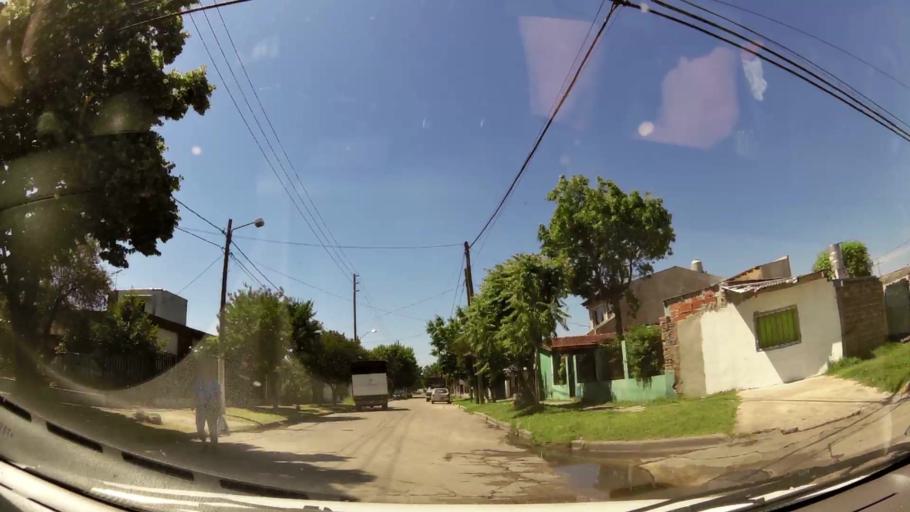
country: AR
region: Buenos Aires
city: Ituzaingo
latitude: -34.6761
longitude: -58.6680
